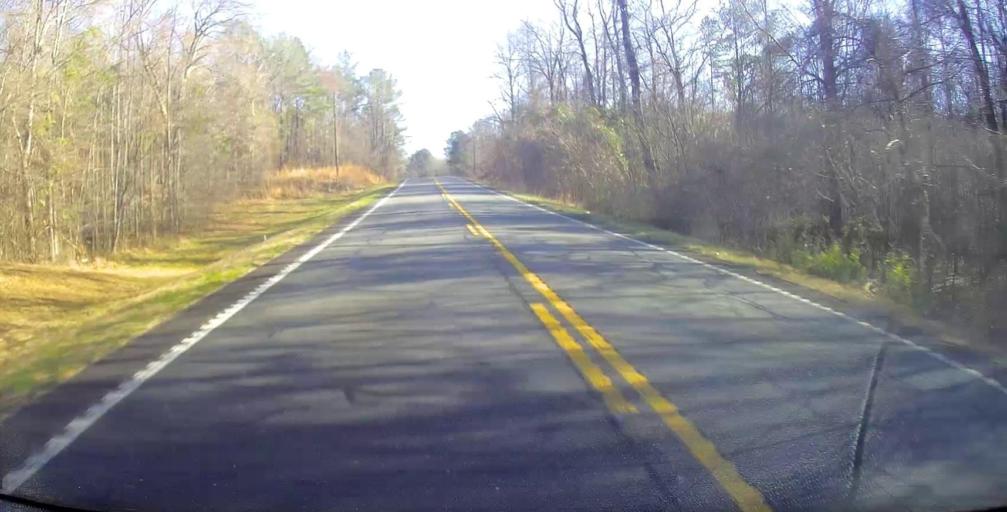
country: US
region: Georgia
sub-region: Talbot County
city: Talbotton
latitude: 32.7028
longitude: -84.5528
